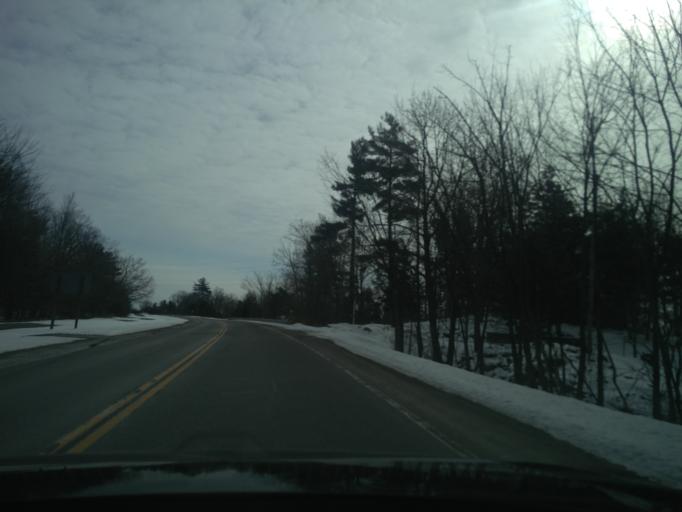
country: US
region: New York
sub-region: Jefferson County
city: Alexandria Bay
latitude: 44.3683
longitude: -75.9717
